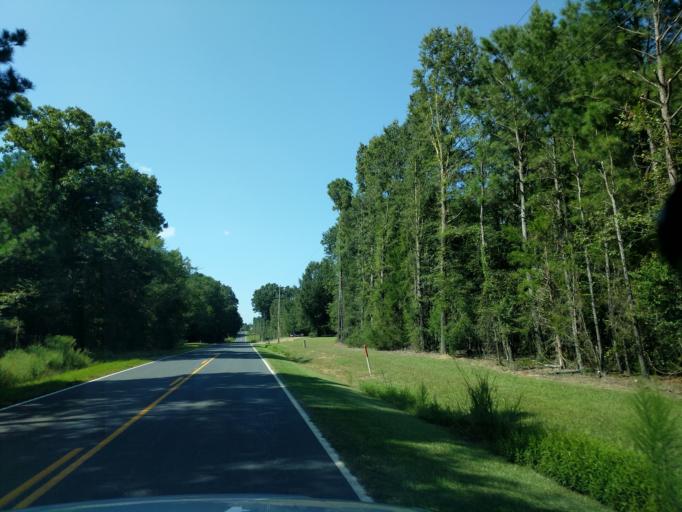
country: US
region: South Carolina
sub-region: Lexington County
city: Leesville
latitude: 34.0361
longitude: -81.5393
